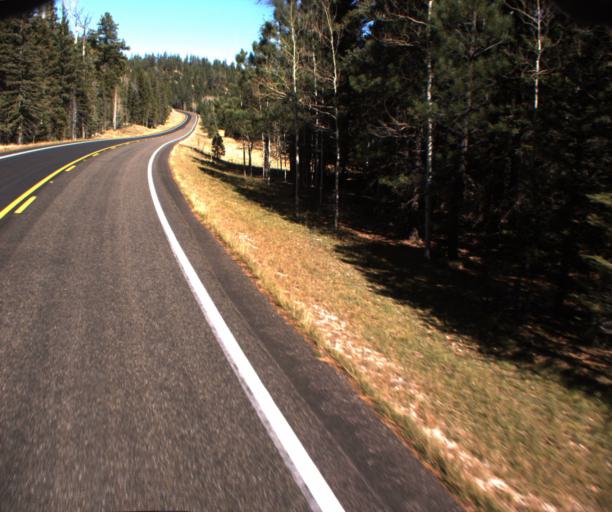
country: US
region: Arizona
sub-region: Coconino County
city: Grand Canyon
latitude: 36.5067
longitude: -112.1405
